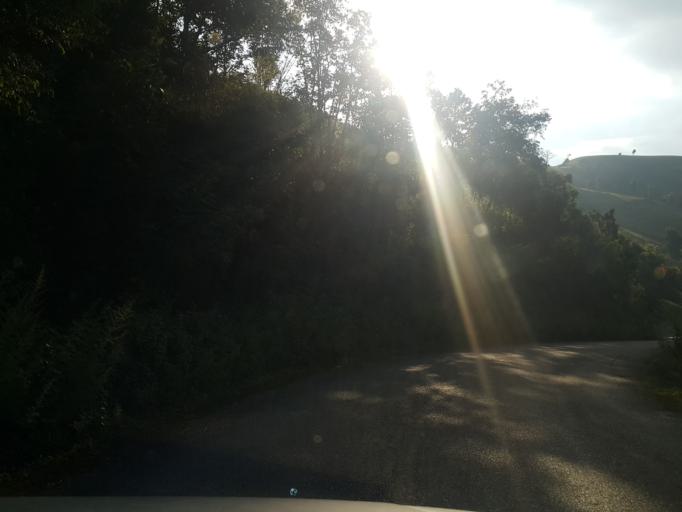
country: TH
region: Chiang Mai
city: Mae Chaem
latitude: 18.7442
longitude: 98.2130
